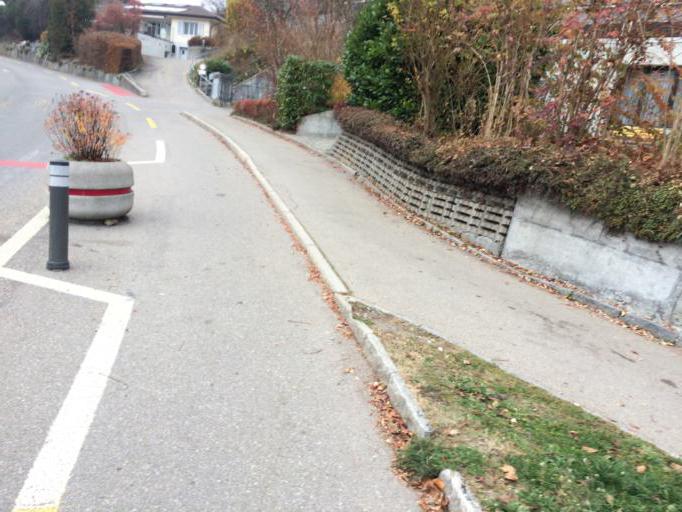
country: CH
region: Bern
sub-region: Bern-Mittelland District
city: Kehrsatz
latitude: 46.9078
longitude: 7.4660
